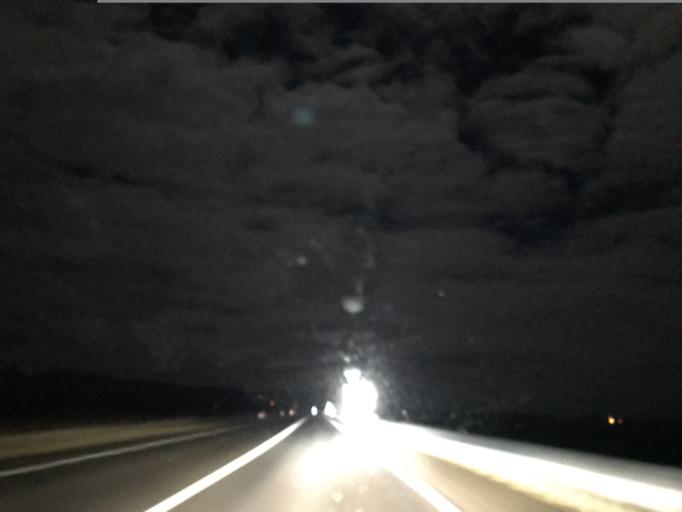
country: FR
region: Auvergne
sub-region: Departement de l'Allier
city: Saint-Yorre
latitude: 46.0565
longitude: 3.4486
